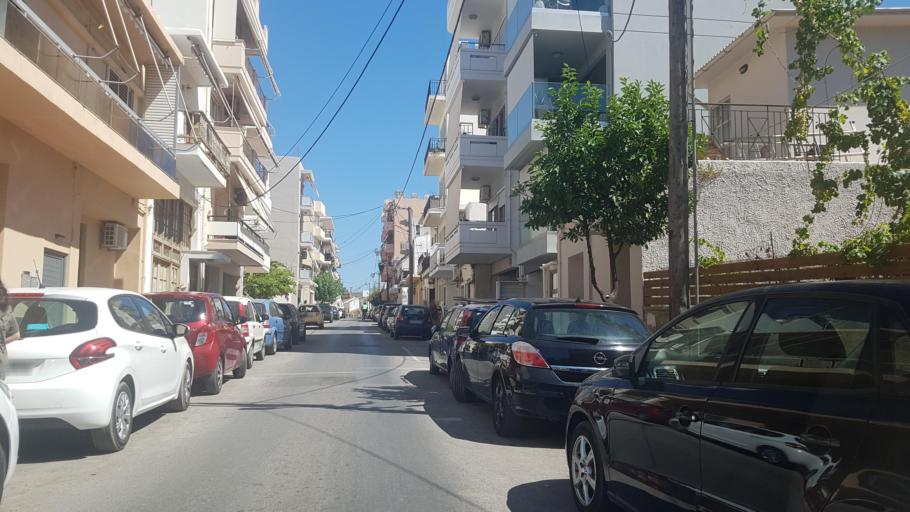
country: GR
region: Crete
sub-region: Nomos Chanias
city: Chania
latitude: 35.5152
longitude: 24.0091
